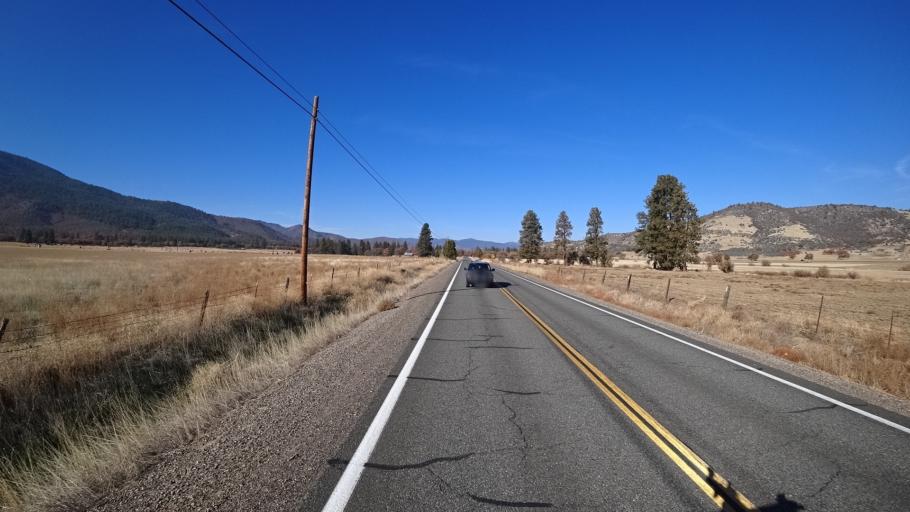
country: US
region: California
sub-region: Siskiyou County
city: Montague
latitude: 41.6557
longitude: -122.5793
